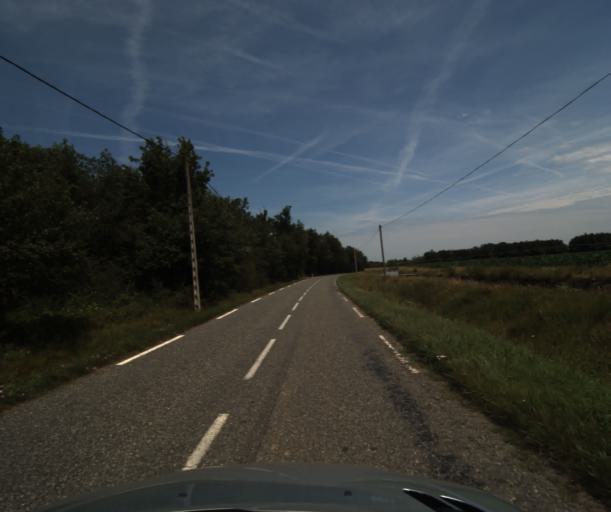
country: FR
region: Midi-Pyrenees
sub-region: Departement de la Haute-Garonne
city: Lherm
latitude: 43.4442
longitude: 1.2276
